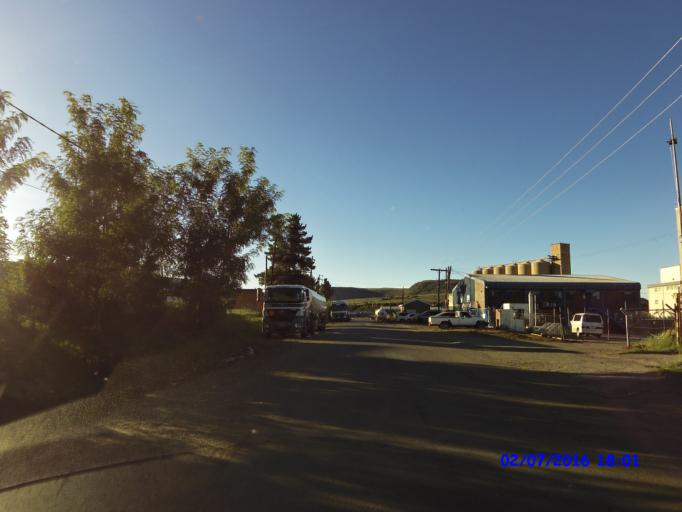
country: LS
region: Maseru
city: Maseru
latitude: -29.2986
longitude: 27.4817
